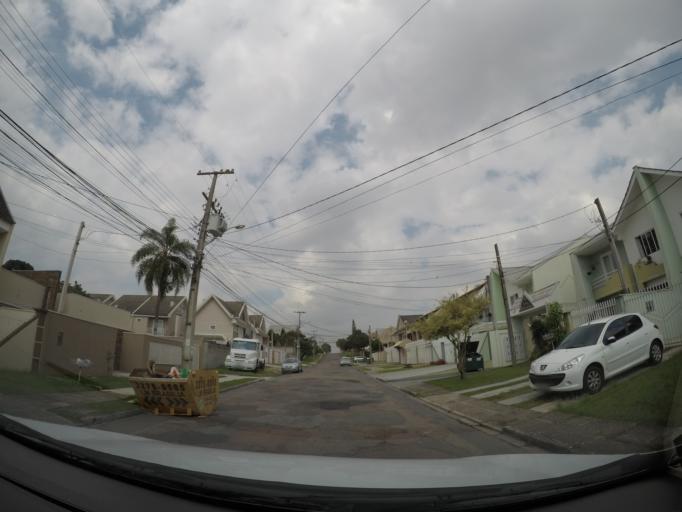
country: BR
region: Parana
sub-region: Sao Jose Dos Pinhais
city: Sao Jose dos Pinhais
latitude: -25.4964
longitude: -49.2511
